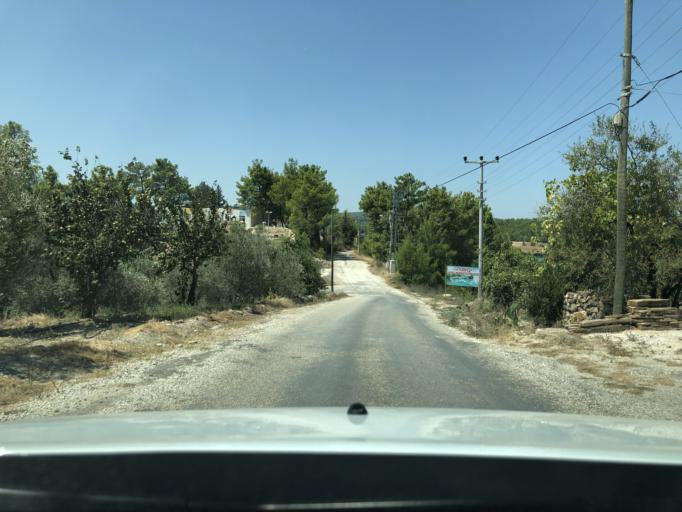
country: TR
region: Antalya
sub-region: Manavgat
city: Kizilagac
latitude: 36.8581
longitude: 31.5550
